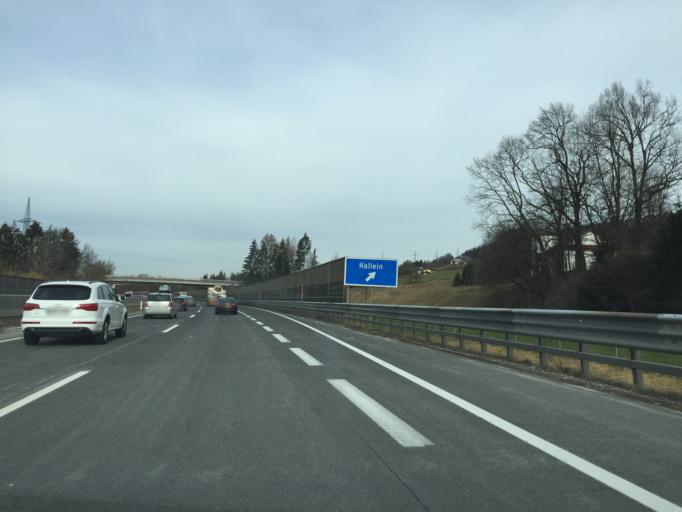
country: AT
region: Salzburg
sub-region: Politischer Bezirk Hallein
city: Adnet
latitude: 47.6852
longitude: 13.1184
